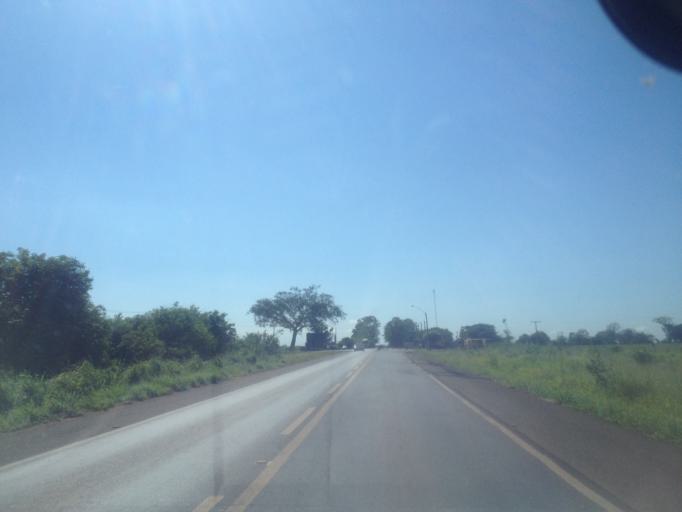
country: BR
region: Minas Gerais
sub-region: Santa Vitoria
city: Santa Vitoria
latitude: -18.9762
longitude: -50.5975
